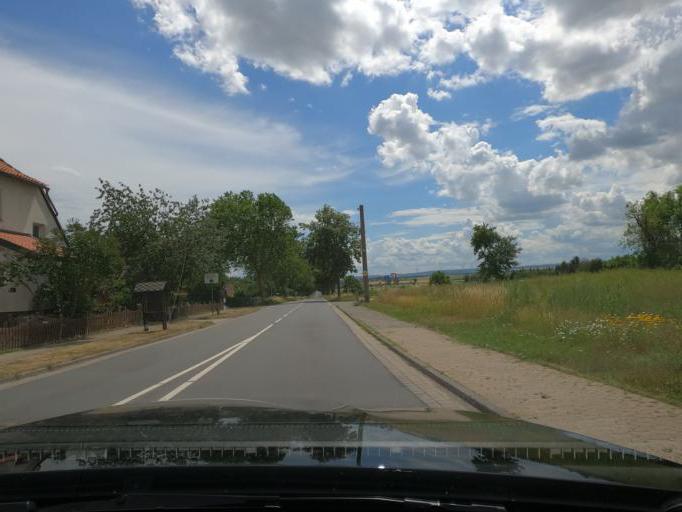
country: DE
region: Lower Saxony
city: Hohenhameln
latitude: 52.2470
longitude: 10.0268
